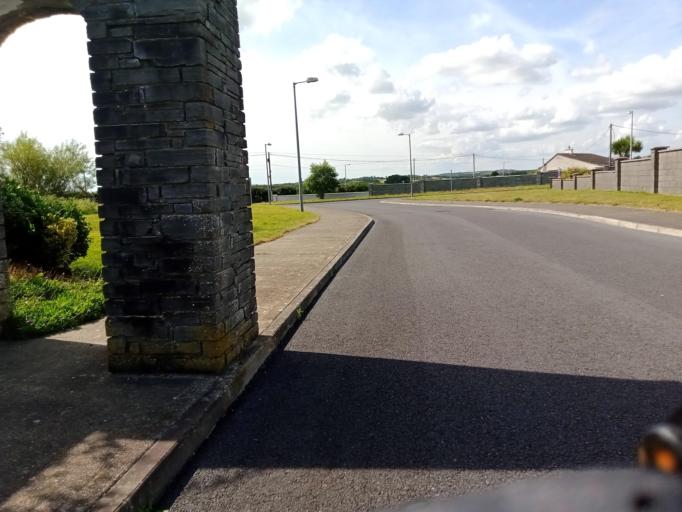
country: IE
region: Munster
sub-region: Waterford
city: Dungarvan
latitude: 52.1296
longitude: -7.4539
